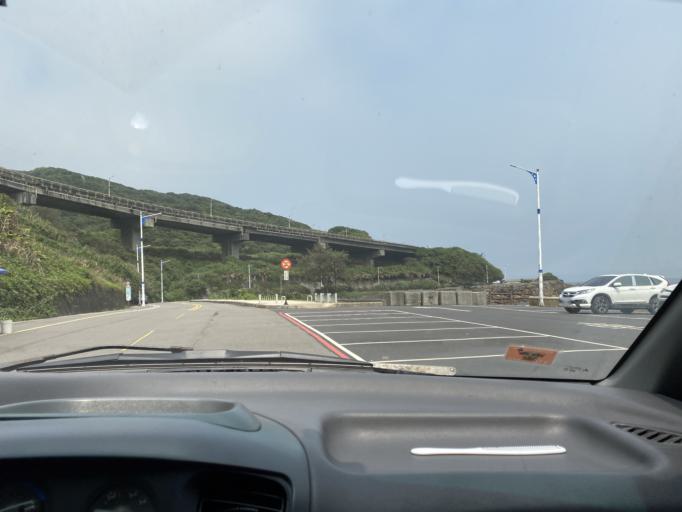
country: TW
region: Taiwan
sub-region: Keelung
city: Keelung
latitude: 25.1677
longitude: 121.7076
